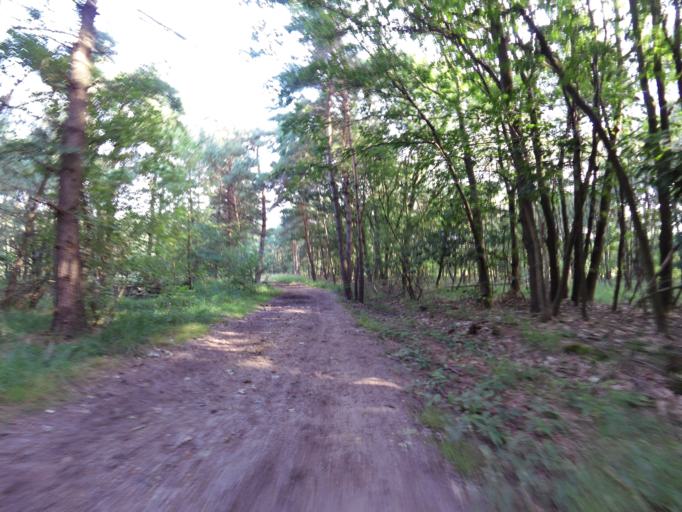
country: NL
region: North Brabant
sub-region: Gemeente Son en Breugel
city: Son
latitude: 51.5116
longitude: 5.4473
